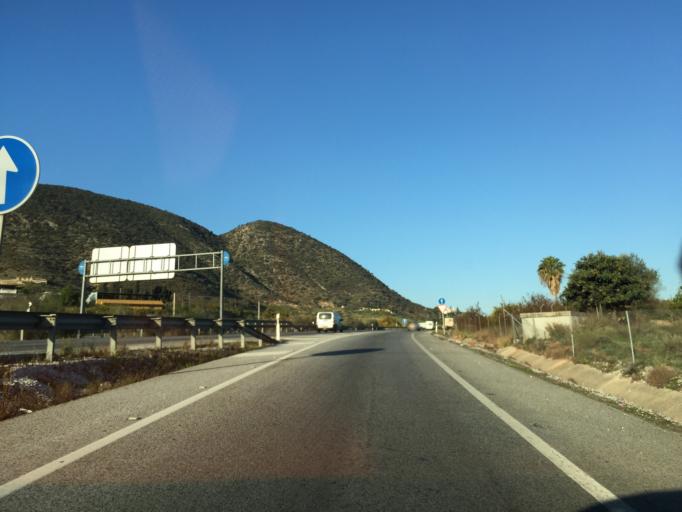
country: ES
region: Andalusia
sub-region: Provincia de Malaga
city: Estacion de Cartama
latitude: 36.7187
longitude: -4.5933
